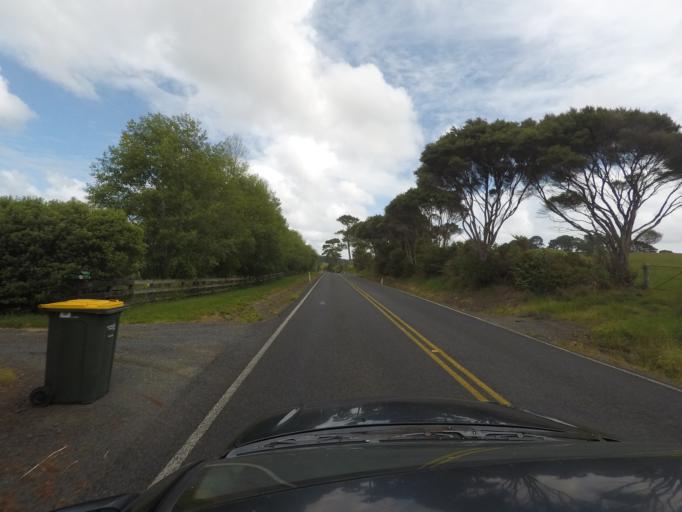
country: NZ
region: Auckland
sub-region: Auckland
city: Parakai
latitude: -36.6516
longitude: 174.5210
